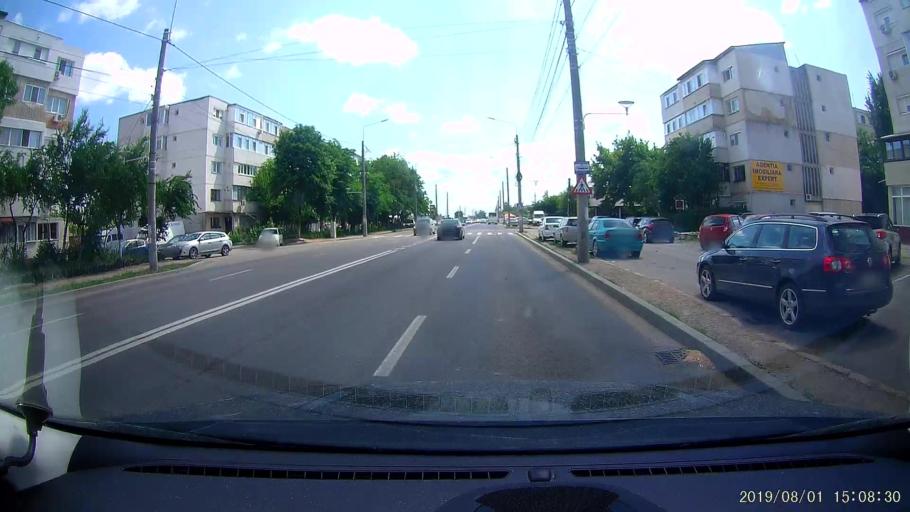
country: RO
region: Braila
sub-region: Municipiul Braila
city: Braila
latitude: 45.2409
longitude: 27.9449
